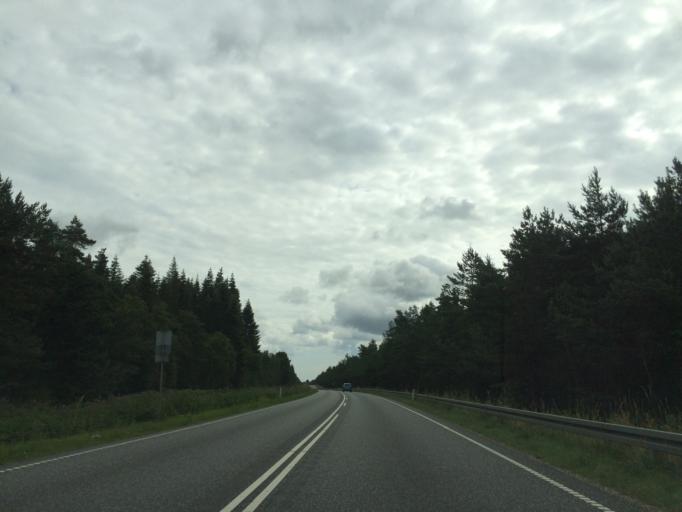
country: DK
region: Central Jutland
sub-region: Syddjurs Kommune
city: Ebeltoft
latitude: 56.2929
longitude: 10.6171
